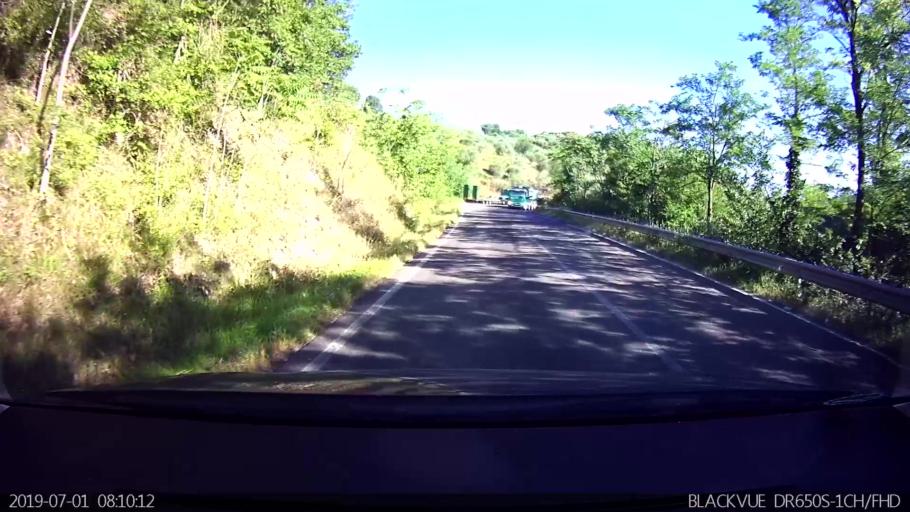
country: IT
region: Latium
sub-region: Provincia di Frosinone
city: Sant'Angelo in Villa-Giglio
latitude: 41.6691
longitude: 13.4221
